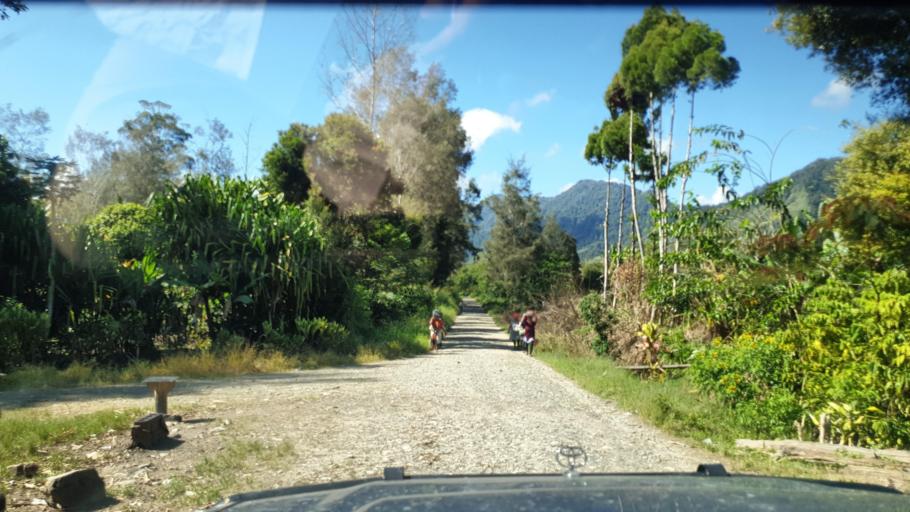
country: PG
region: Western Highlands
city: Rauna
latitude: -5.8144
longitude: 144.3792
